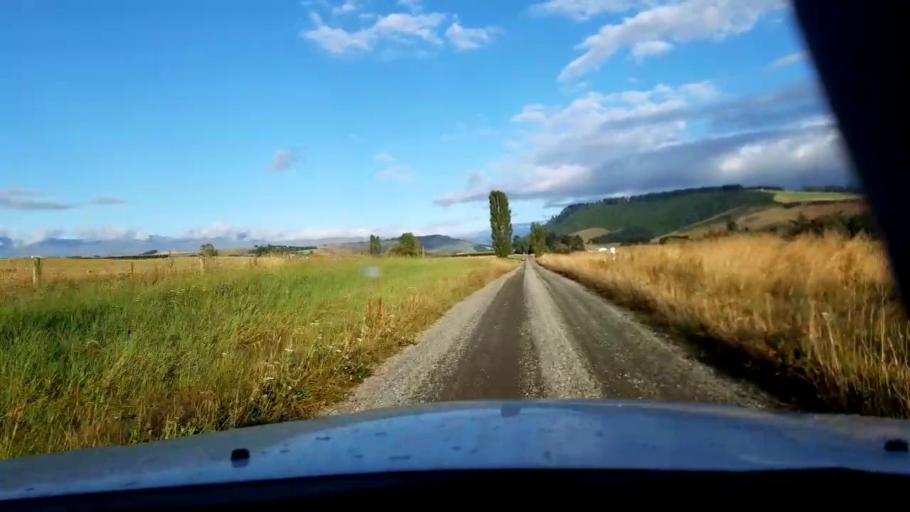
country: NZ
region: Canterbury
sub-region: Timaru District
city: Timaru
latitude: -44.4257
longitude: 171.1139
